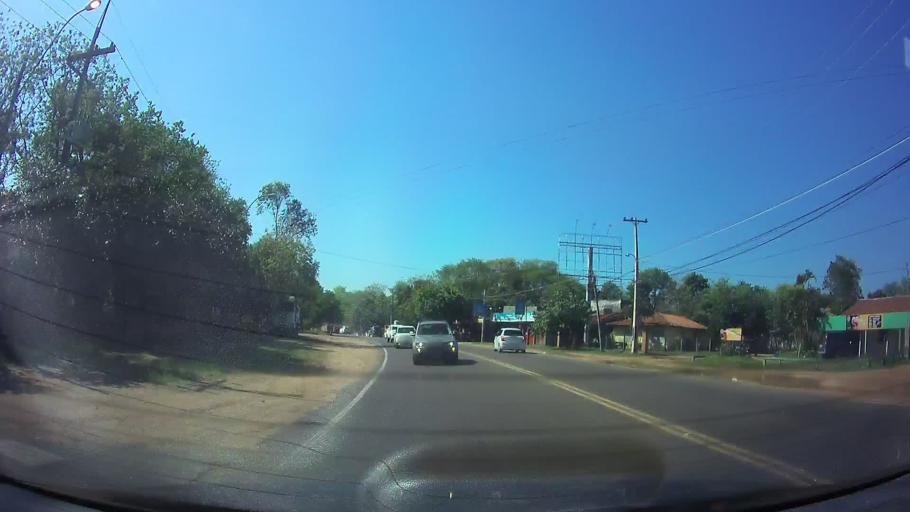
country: PY
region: Cordillera
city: San Bernardino
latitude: -25.3367
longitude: -57.2727
